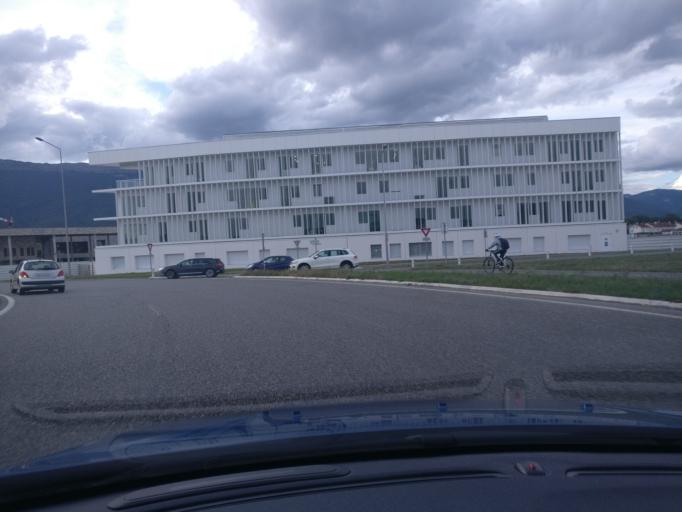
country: FR
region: Rhone-Alpes
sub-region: Departement de l'Ain
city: Saint-Genis-Pouilly
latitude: 46.2400
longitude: 6.0340
